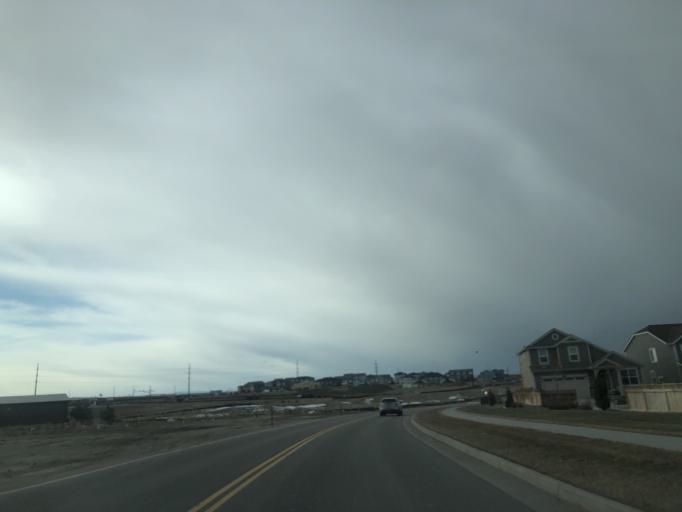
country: US
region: Colorado
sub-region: Douglas County
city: Stonegate
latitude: 39.5541
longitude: -104.8005
